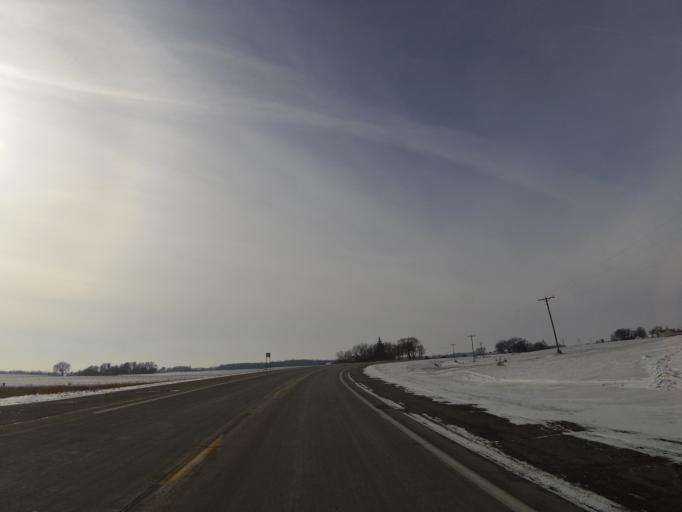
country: US
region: Minnesota
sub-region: McLeod County
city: Hutchinson
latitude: 44.8939
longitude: -94.2262
